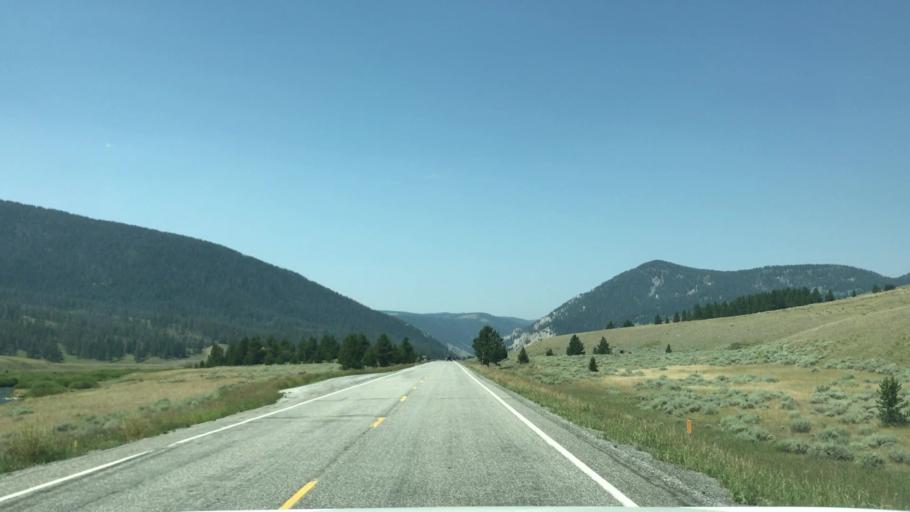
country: US
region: Montana
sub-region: Gallatin County
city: Big Sky
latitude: 45.0464
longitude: -111.1354
